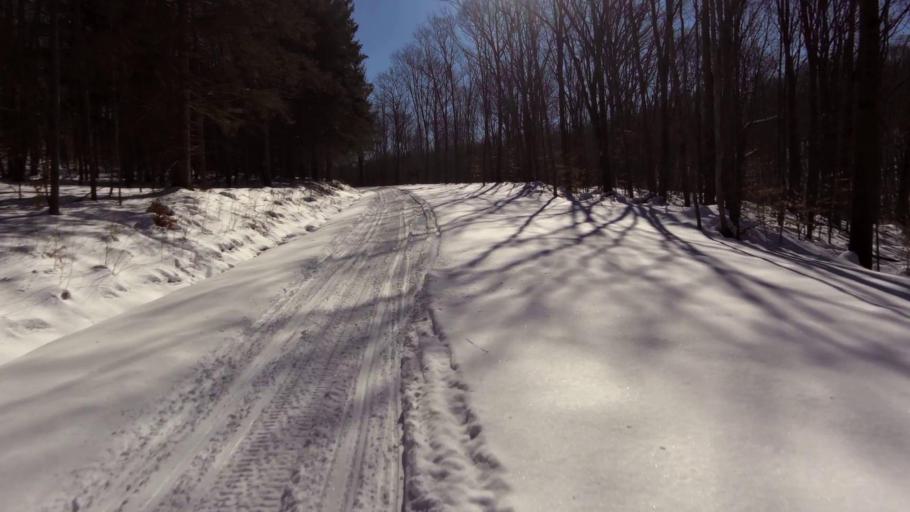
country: US
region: New York
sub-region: Allegany County
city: Cuba
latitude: 42.3049
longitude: -78.2645
